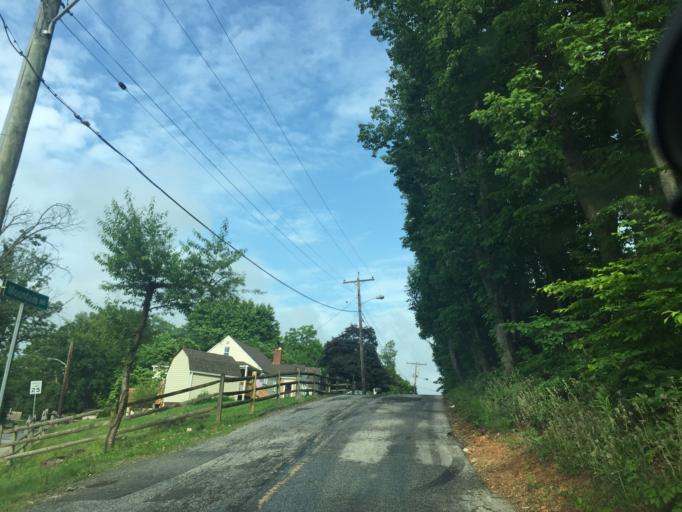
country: US
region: Maryland
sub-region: Baltimore County
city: Parkville
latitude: 39.4027
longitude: -76.5497
